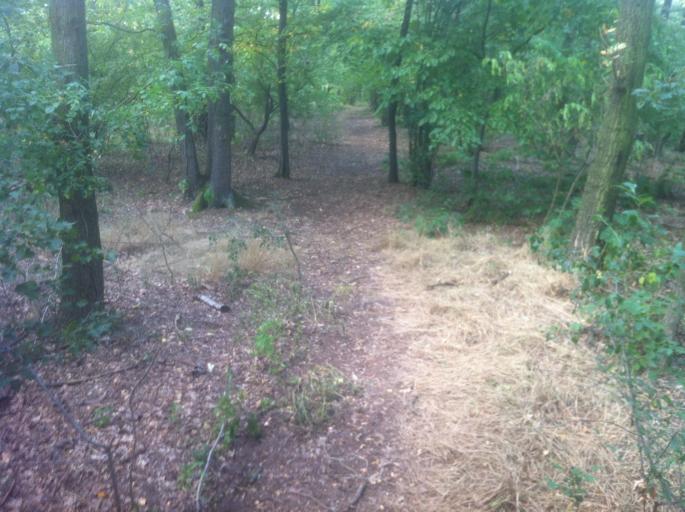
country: DE
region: Saxony
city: Niederau
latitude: 51.1456
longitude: 13.5189
